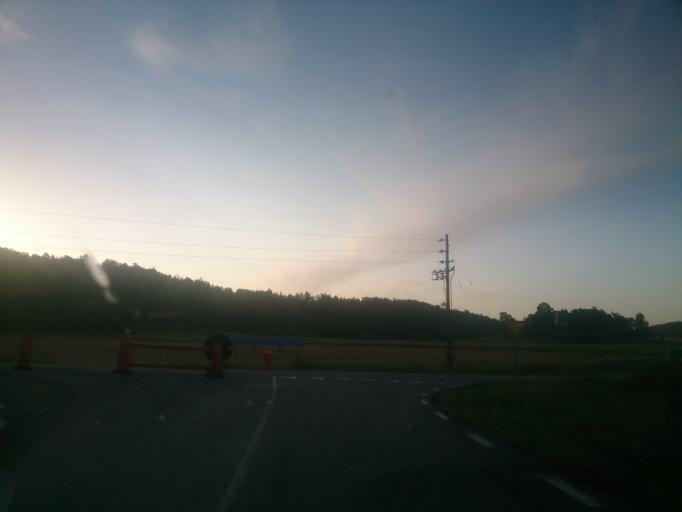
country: SE
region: Soedermanland
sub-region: Nykopings Kommun
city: Nykoping
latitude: 58.8665
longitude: 17.1792
